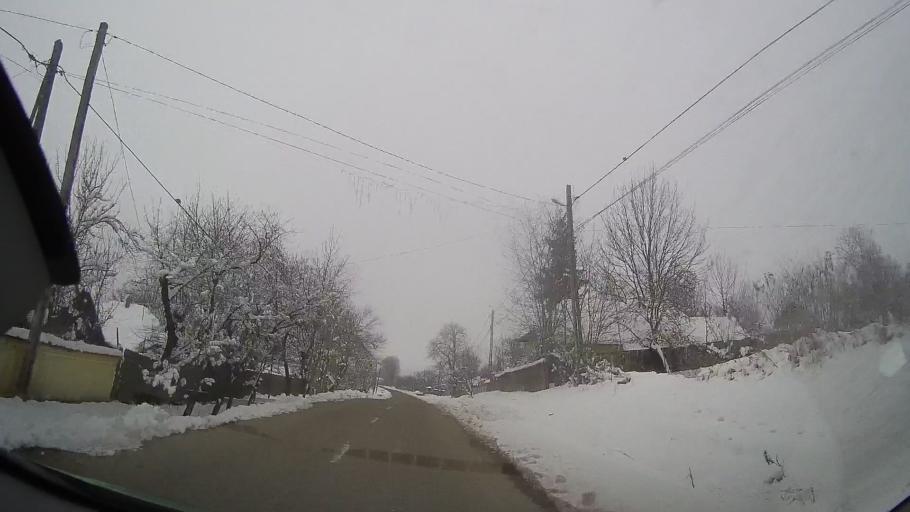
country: RO
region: Neamt
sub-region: Comuna Bozieni
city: Bozieni
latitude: 46.8290
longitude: 27.1830
